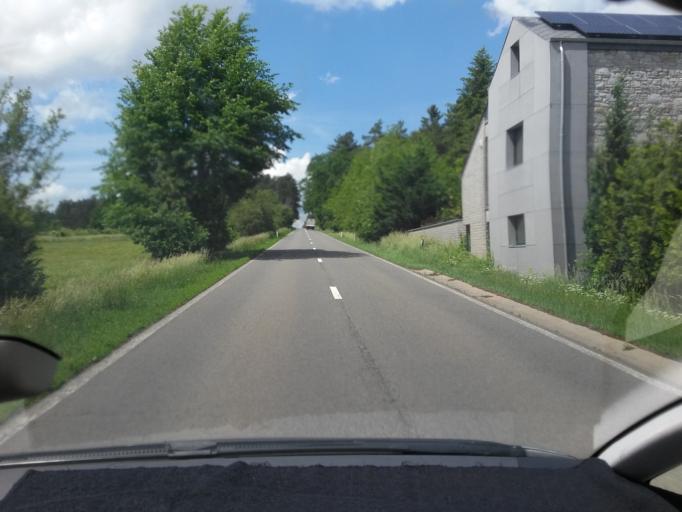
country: BE
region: Wallonia
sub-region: Province de Namur
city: Rochefort
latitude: 50.1312
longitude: 5.2352
